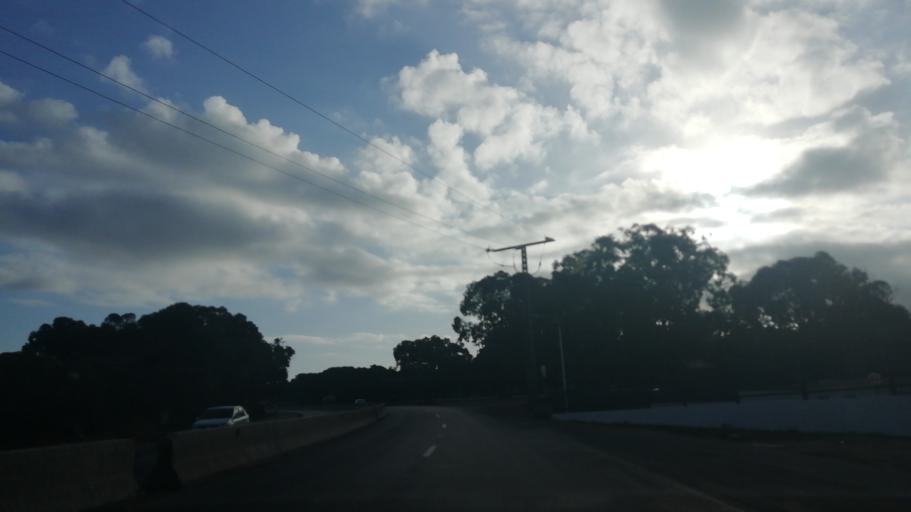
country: DZ
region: Mostaganem
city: Mostaganem
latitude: 36.1130
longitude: 0.2364
